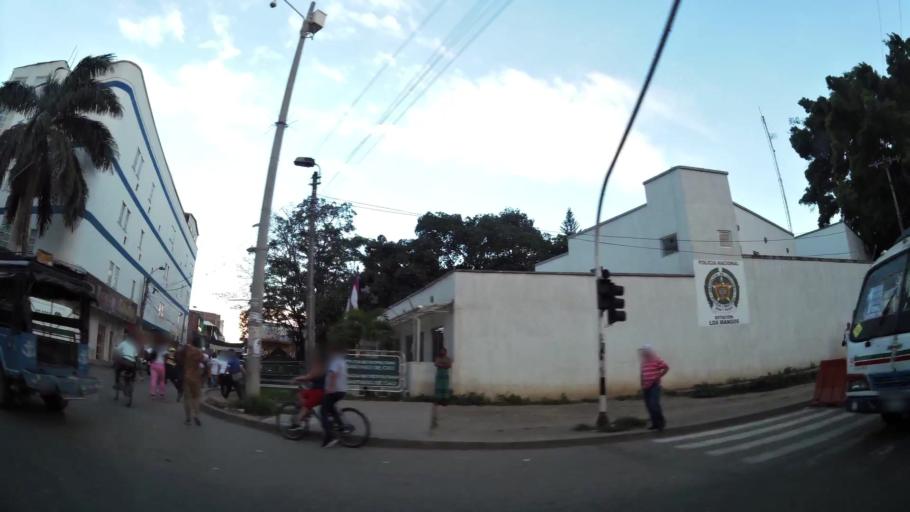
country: CO
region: Valle del Cauca
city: Cali
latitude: 3.4270
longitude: -76.4841
